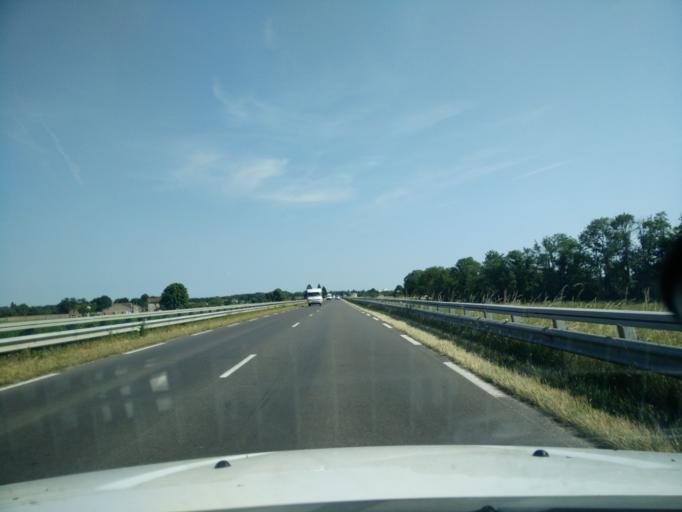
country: FR
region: Auvergne
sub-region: Departement de l'Allier
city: Moulins
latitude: 46.5436
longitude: 3.3200
